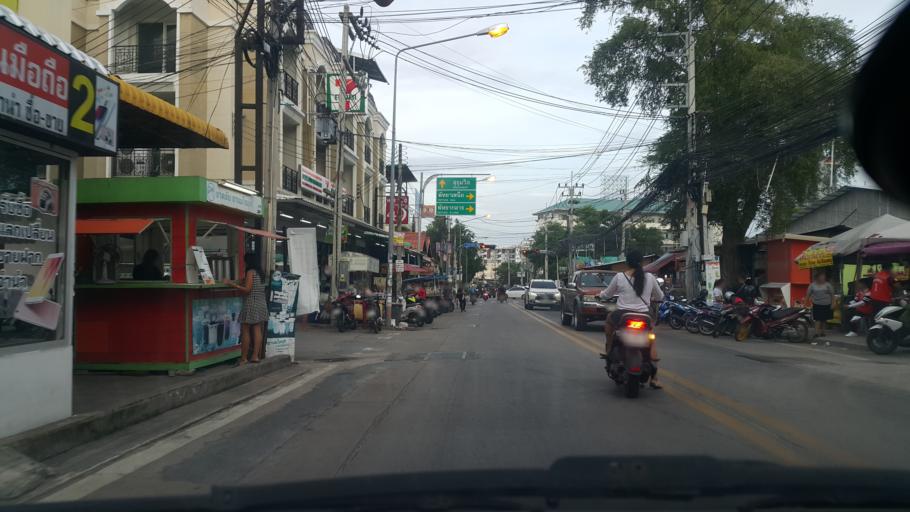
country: TH
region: Chon Buri
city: Phatthaya
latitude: 12.9560
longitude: 100.8985
